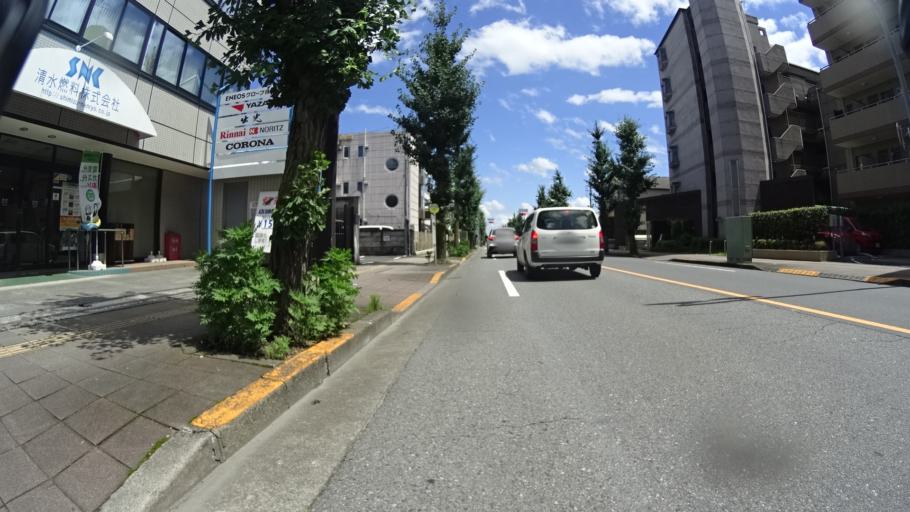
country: JP
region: Tokyo
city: Ome
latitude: 35.7844
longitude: 139.2815
